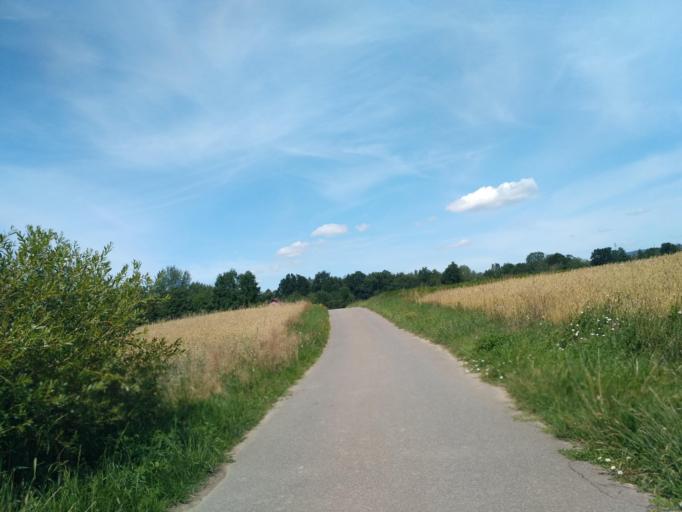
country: PL
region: Subcarpathian Voivodeship
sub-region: Powiat brzozowski
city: Jablonica Polska
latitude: 49.6901
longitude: 21.8802
